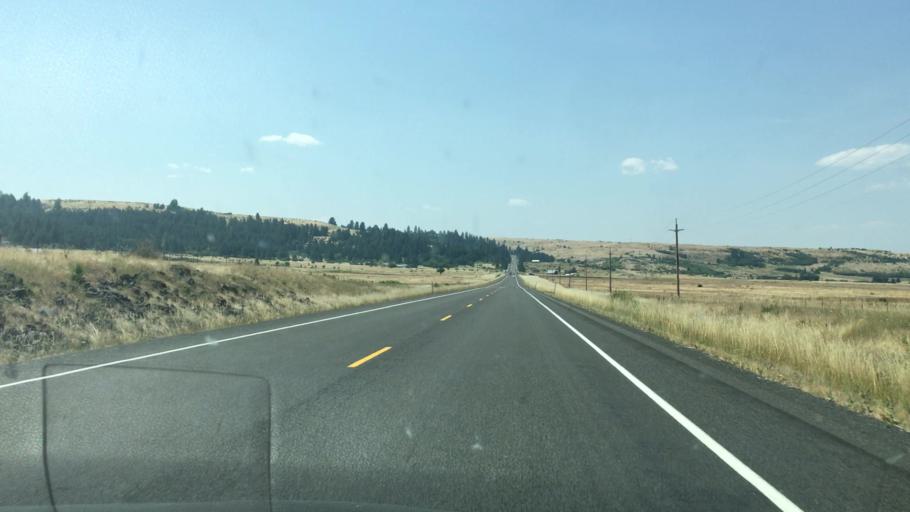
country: US
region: Idaho
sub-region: Idaho County
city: Grangeville
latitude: 45.8863
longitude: -116.2047
